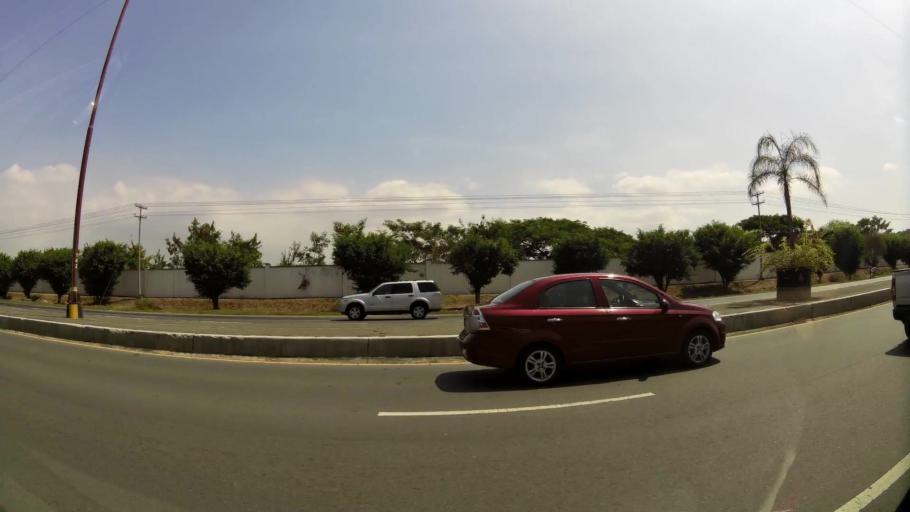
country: EC
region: Guayas
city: Eloy Alfaro
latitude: -2.0879
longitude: -79.8735
